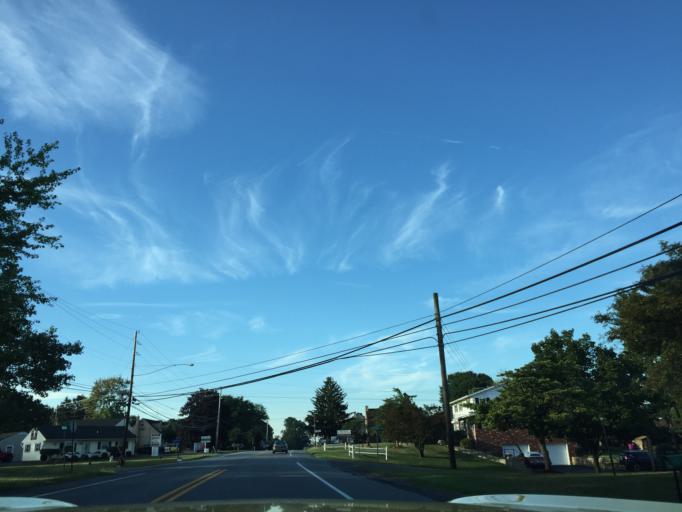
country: US
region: Pennsylvania
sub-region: Lehigh County
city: Dorneyville
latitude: 40.5756
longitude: -75.5201
